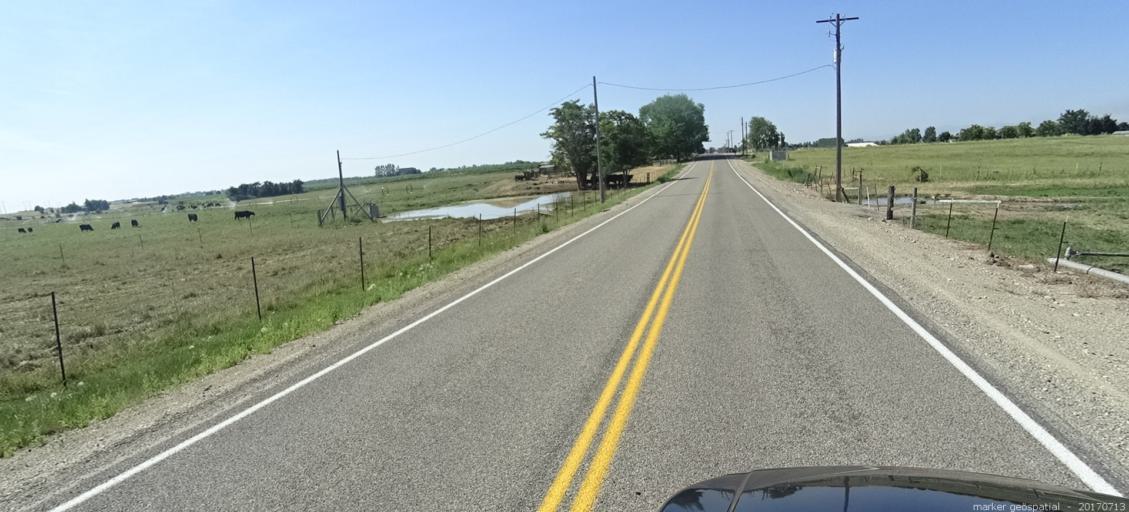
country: US
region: Idaho
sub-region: Ada County
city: Kuna
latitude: 43.5262
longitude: -116.3743
